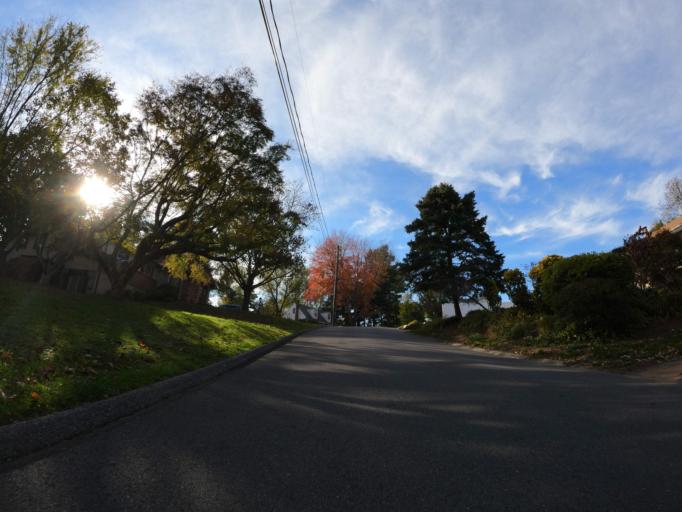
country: US
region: Maryland
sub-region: Carroll County
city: Sykesville
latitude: 39.3712
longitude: -76.9720
